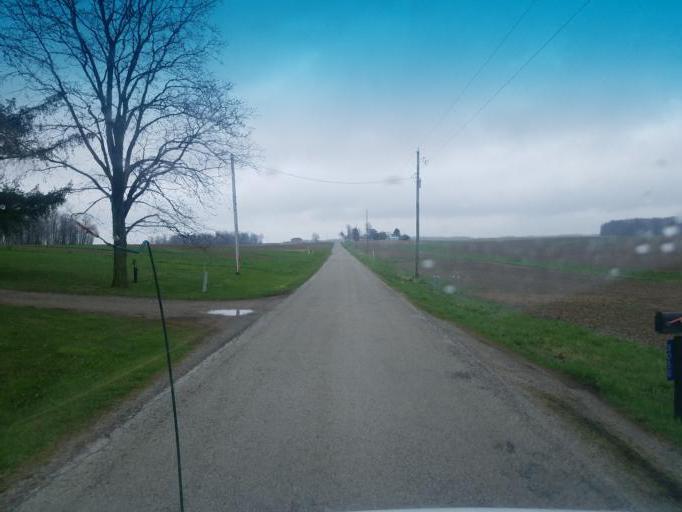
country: US
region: Ohio
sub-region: Huron County
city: Plymouth
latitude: 40.9634
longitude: -82.7315
